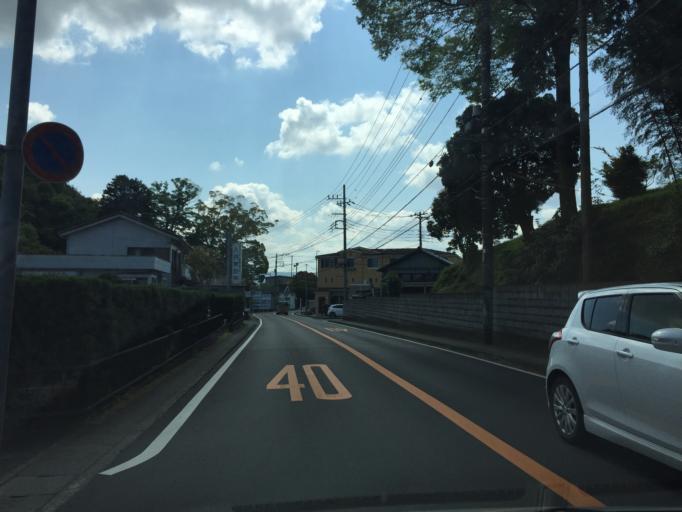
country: JP
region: Shizuoka
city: Numazu
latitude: 35.0939
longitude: 138.8936
